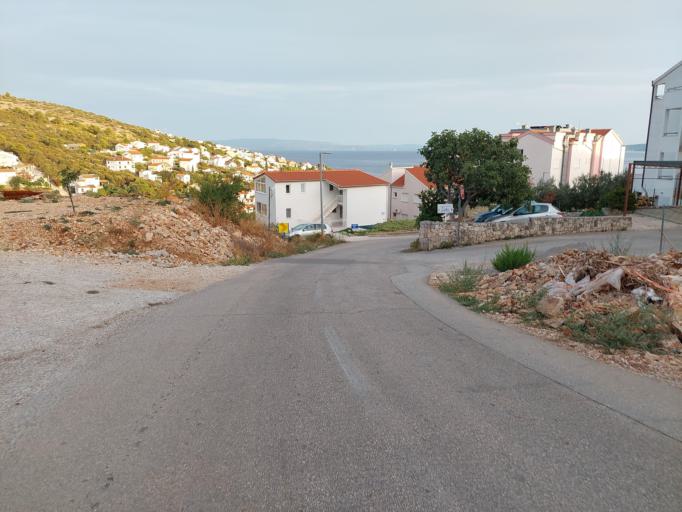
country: HR
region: Splitsko-Dalmatinska
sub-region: Grad Trogir
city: Trogir
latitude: 43.4956
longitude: 16.2707
